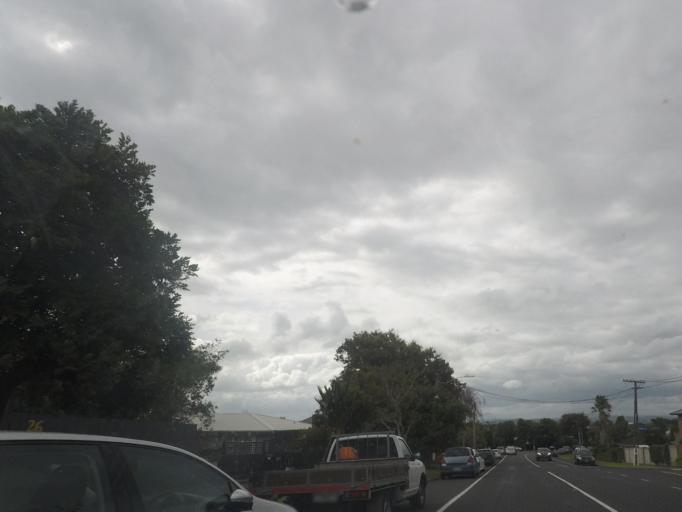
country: NZ
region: Auckland
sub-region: Auckland
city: Tamaki
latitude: -36.8669
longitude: 174.8545
